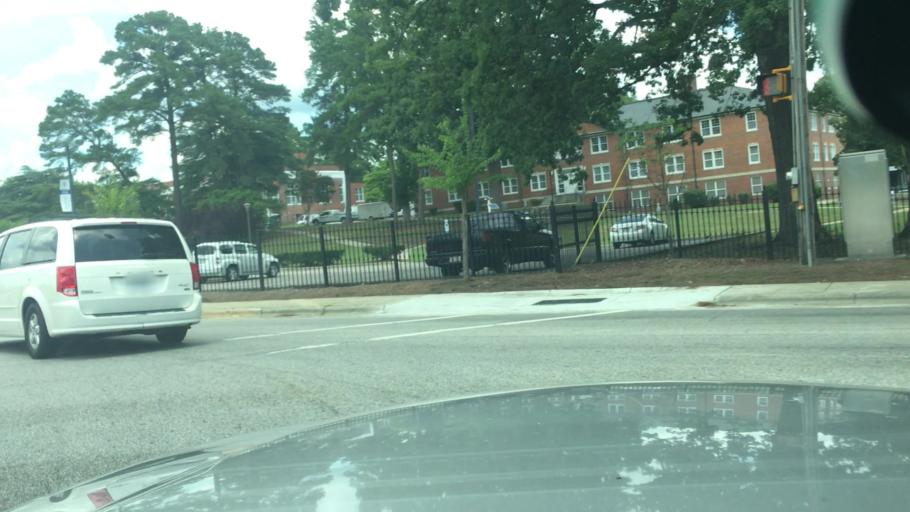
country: US
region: North Carolina
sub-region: Cumberland County
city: Fayetteville
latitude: 35.0693
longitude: -78.8927
